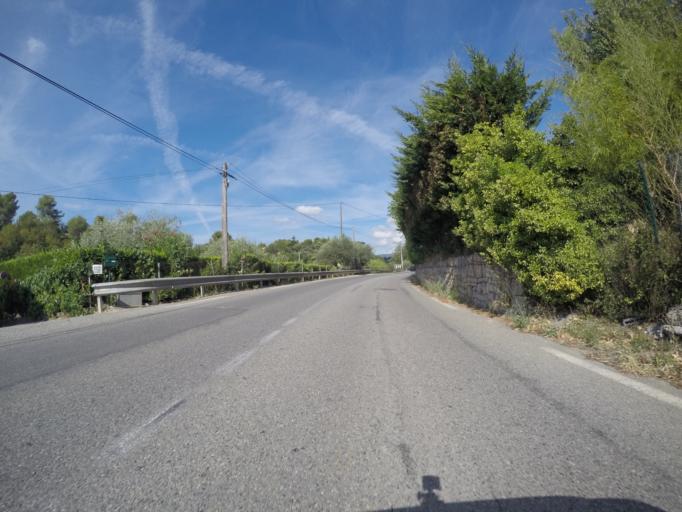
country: FR
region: Provence-Alpes-Cote d'Azur
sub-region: Departement des Alpes-Maritimes
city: Le Rouret
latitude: 43.6752
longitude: 7.0213
